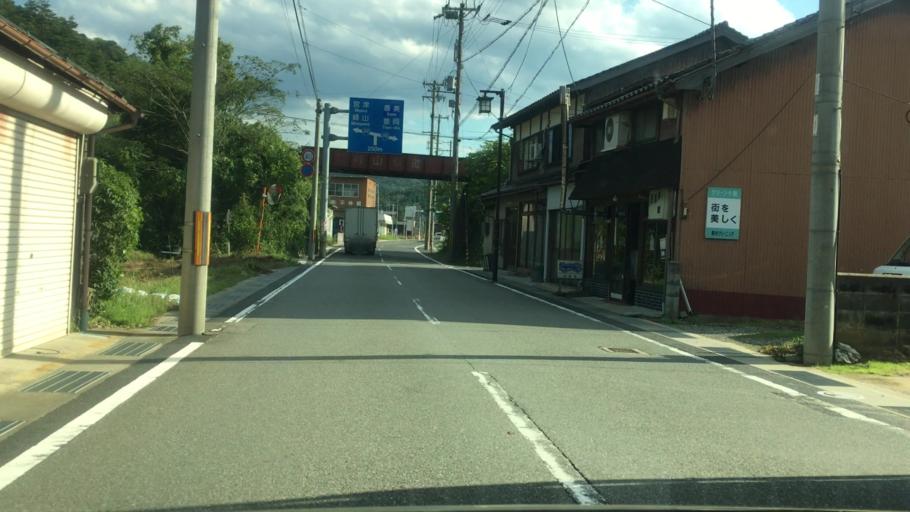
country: JP
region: Hyogo
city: Toyooka
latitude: 35.6041
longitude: 134.9010
